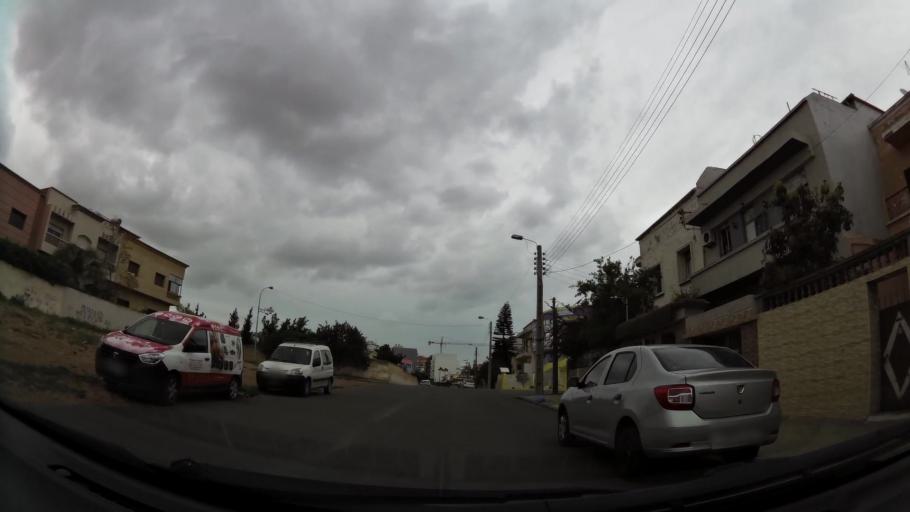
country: MA
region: Grand Casablanca
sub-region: Casablanca
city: Casablanca
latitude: 33.5675
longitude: -7.6173
